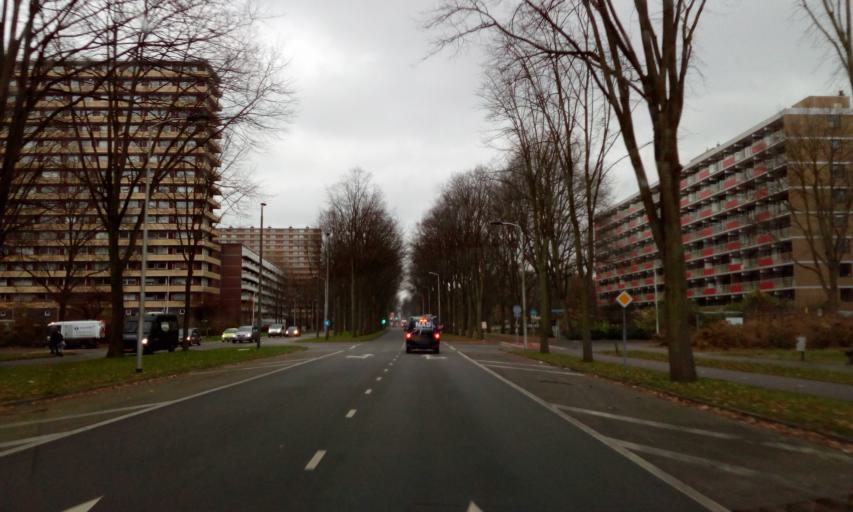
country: NL
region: South Holland
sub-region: Gemeente Delft
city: Delft
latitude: 51.9953
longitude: 4.3551
